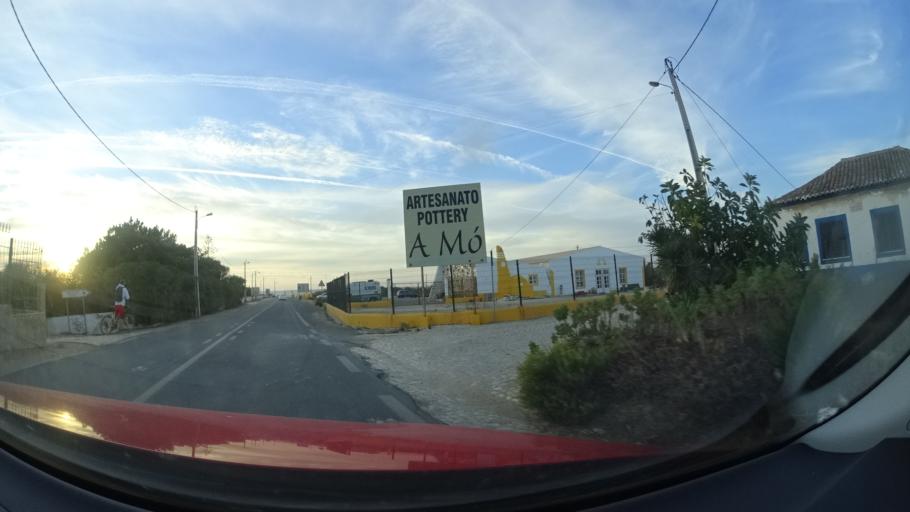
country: PT
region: Faro
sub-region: Vila do Bispo
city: Sagres
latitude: 37.0081
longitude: -8.9463
